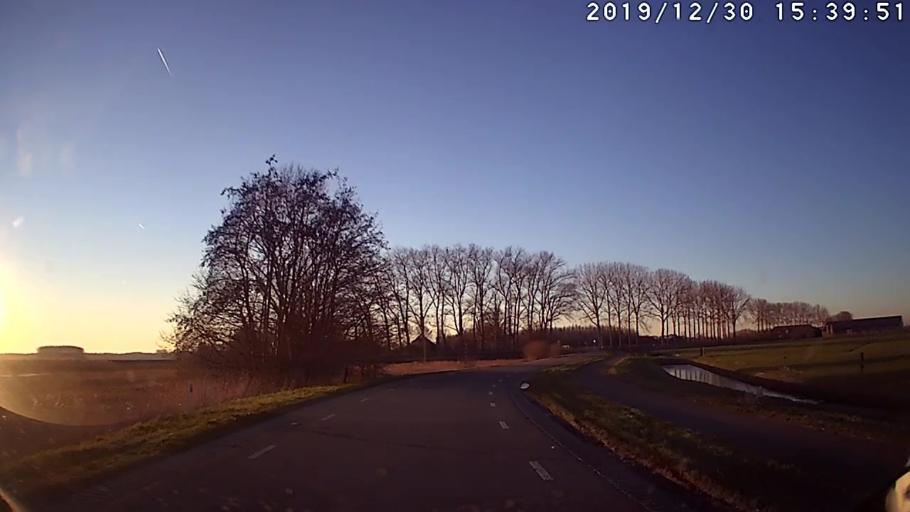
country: NL
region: Overijssel
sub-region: Gemeente Olst-Wijhe
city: Wijhe
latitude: 52.4606
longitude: 6.1549
